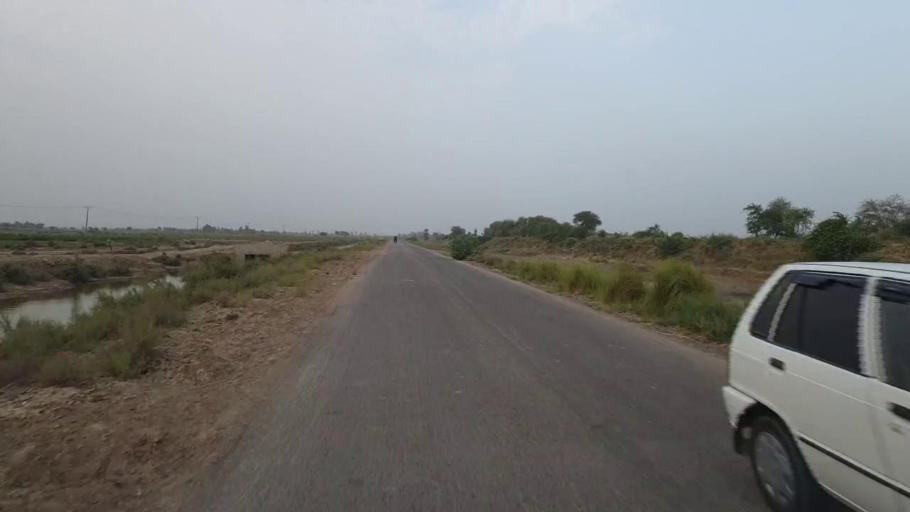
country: PK
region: Sindh
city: Daur
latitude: 26.4437
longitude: 68.2806
